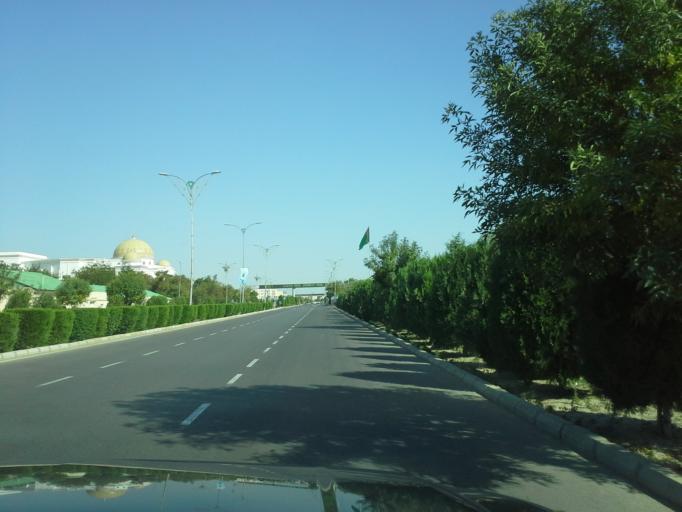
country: TM
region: Dasoguz
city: Dasoguz
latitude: 41.8261
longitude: 59.9566
